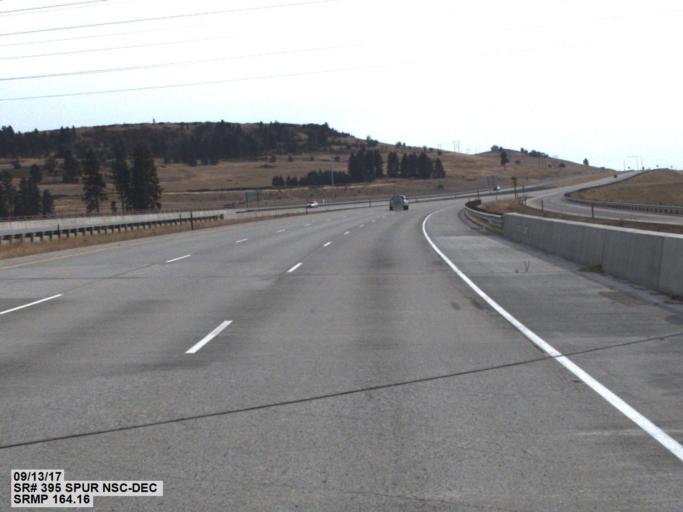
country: US
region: Washington
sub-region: Spokane County
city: Mead
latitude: 47.7521
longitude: -117.3599
